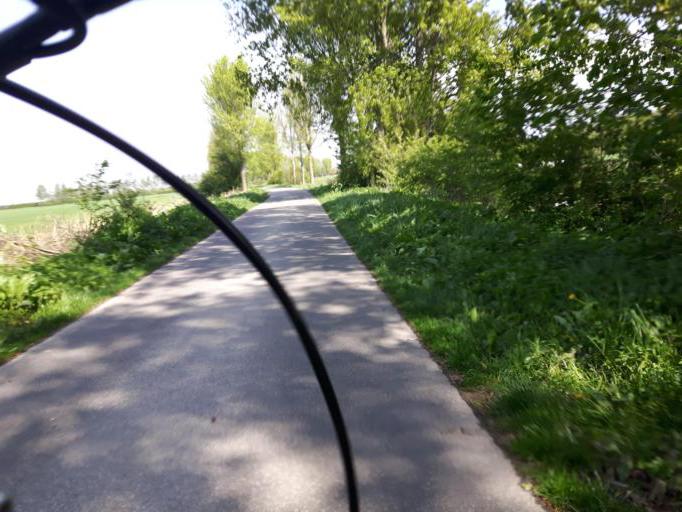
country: NL
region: Zeeland
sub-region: Gemeente Goes
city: Goes
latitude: 51.4500
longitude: 3.8720
